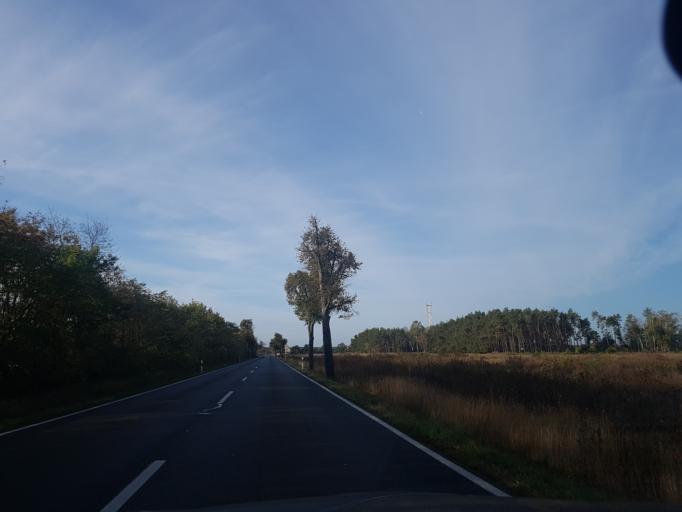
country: DE
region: Saxony
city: Arzberg
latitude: 51.6038
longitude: 13.1321
